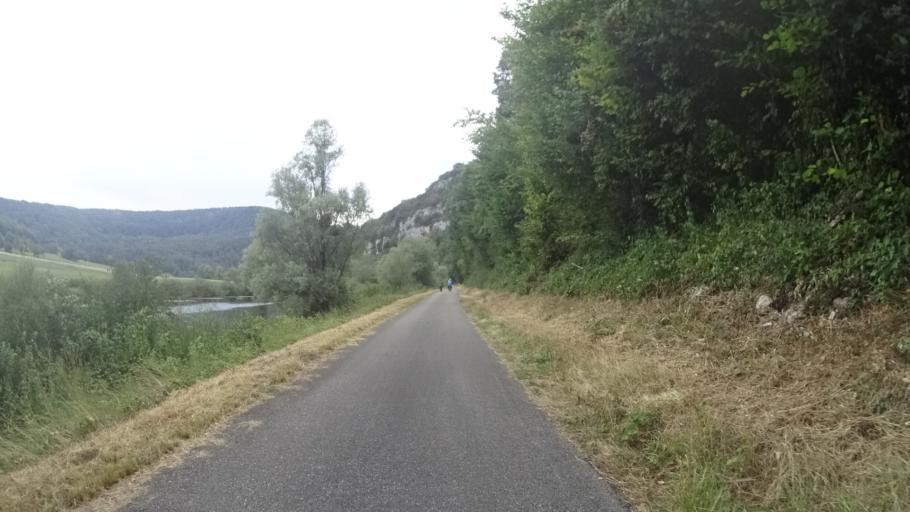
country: FR
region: Franche-Comte
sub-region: Departement du Doubs
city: Baume-les-Dames
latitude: 47.3422
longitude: 6.3200
